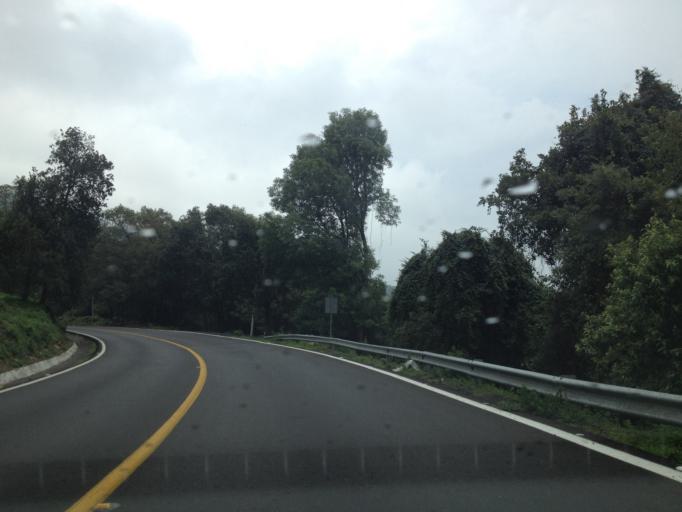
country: MX
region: Michoacan
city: Tingambato
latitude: 19.5082
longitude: -101.8393
